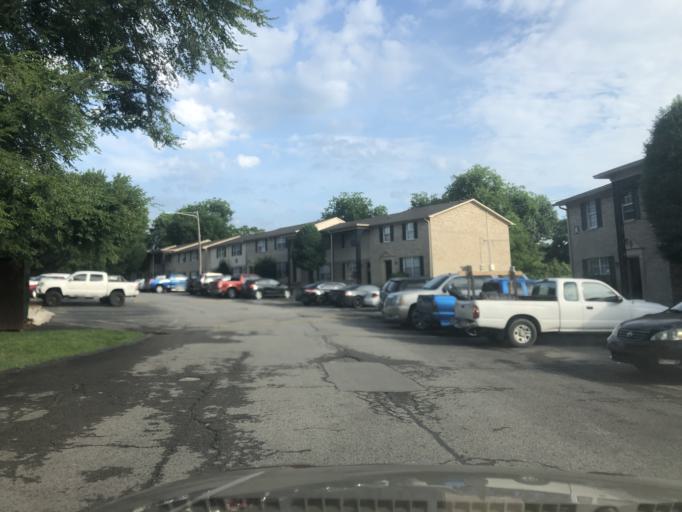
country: US
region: Tennessee
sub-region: Davidson County
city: Goodlettsville
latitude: 36.2464
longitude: -86.7138
